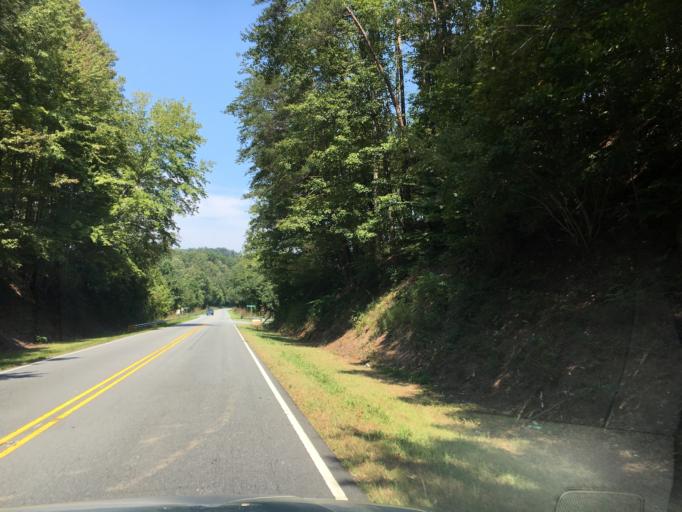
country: US
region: North Carolina
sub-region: Rutherford County
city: Rutherfordton
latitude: 35.5174
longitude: -81.9733
